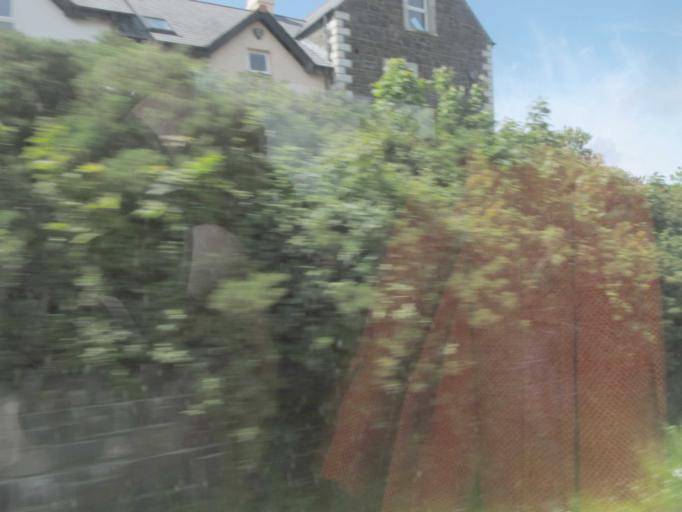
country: GB
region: Northern Ireland
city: Bushmills
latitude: 55.2014
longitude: -6.5271
